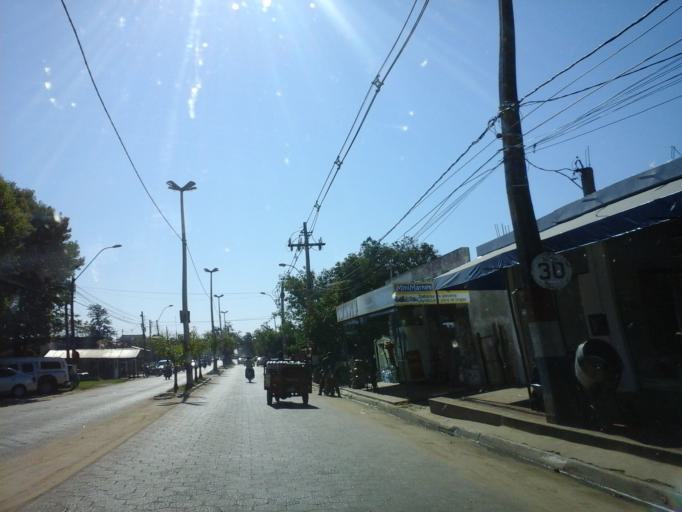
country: PY
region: Neembucu
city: Pilar
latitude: -26.8686
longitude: -58.3021
